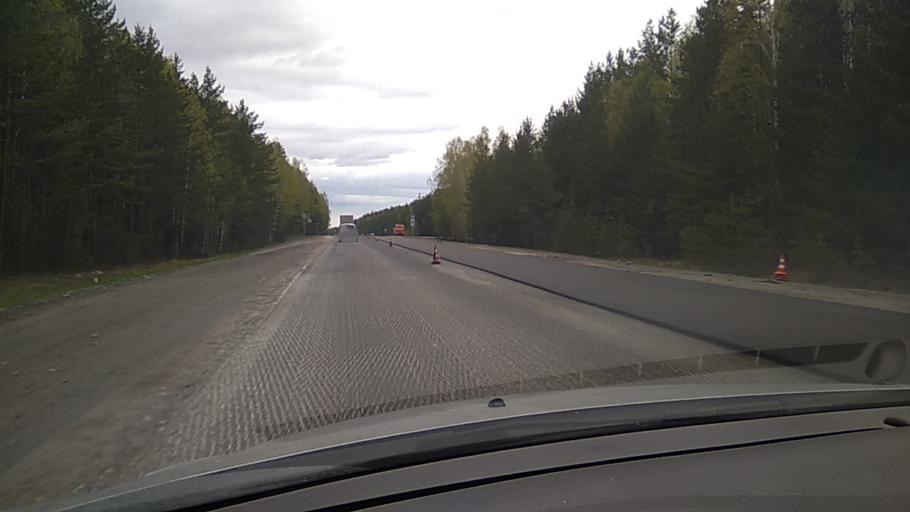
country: RU
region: Sverdlovsk
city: Verkhneye Dubrovo
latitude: 56.6898
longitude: 61.1076
